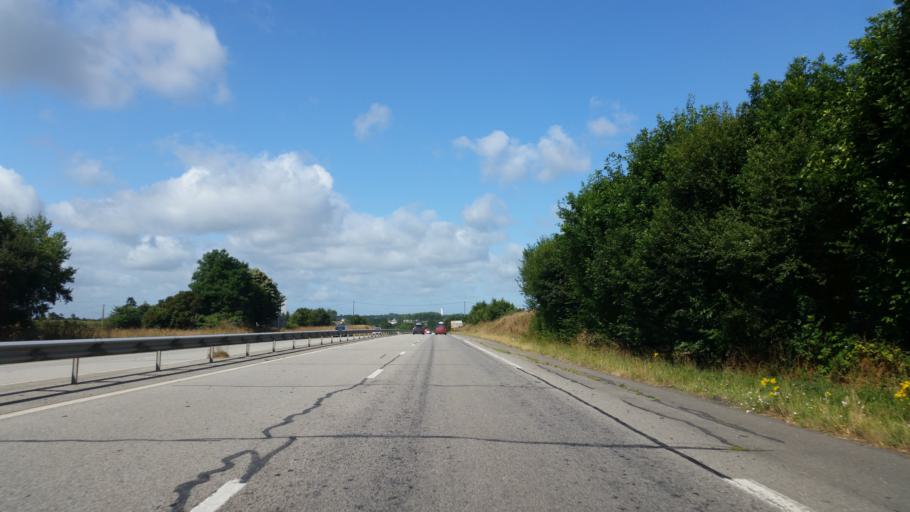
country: FR
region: Lower Normandy
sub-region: Departement du Calvados
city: Isigny-sur-Mer
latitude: 49.3083
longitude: -1.1232
